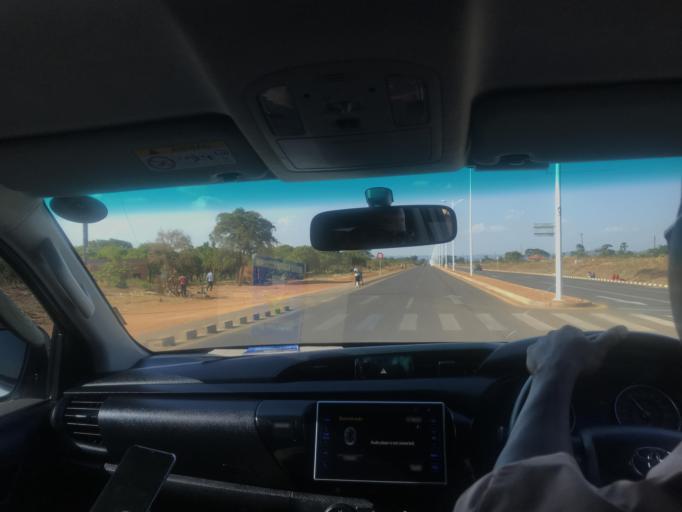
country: ZM
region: Northern
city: Mpika
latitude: -11.8261
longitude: 31.4487
